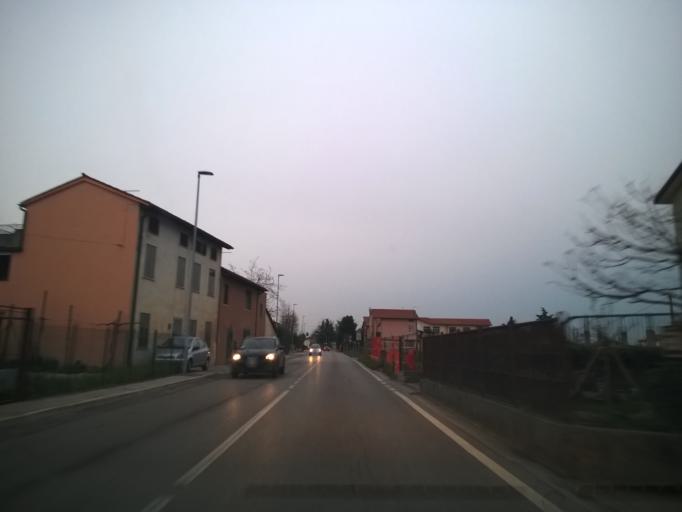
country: IT
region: Veneto
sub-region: Provincia di Vicenza
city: Thiene
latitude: 45.6800
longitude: 11.4769
